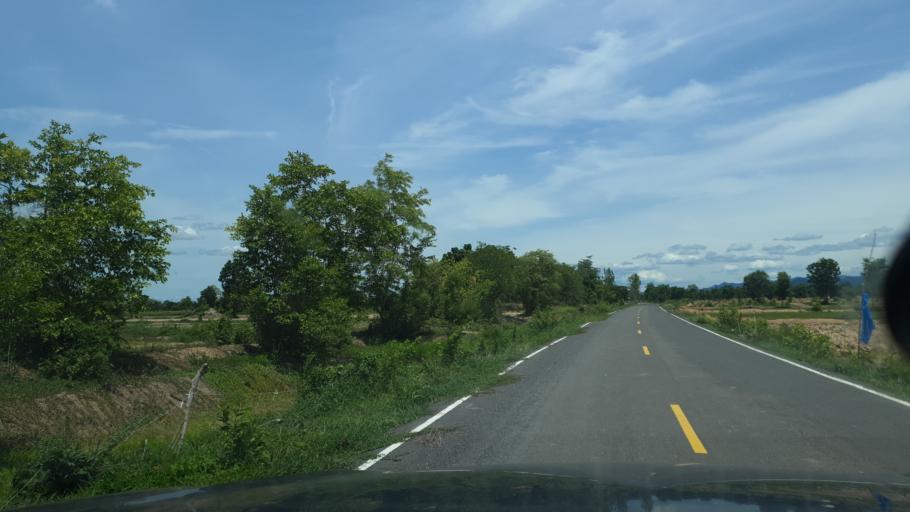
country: TH
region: Sukhothai
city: Ban Na
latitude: 17.1505
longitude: 99.6482
